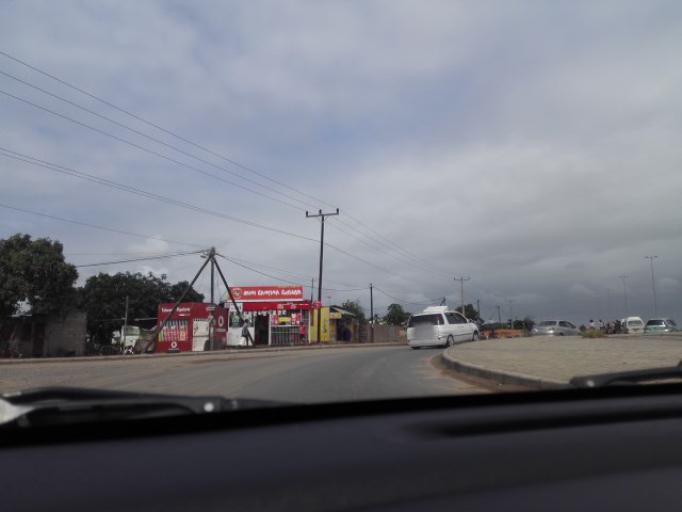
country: MZ
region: Maputo City
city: Maputo
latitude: -25.8265
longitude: 32.6017
